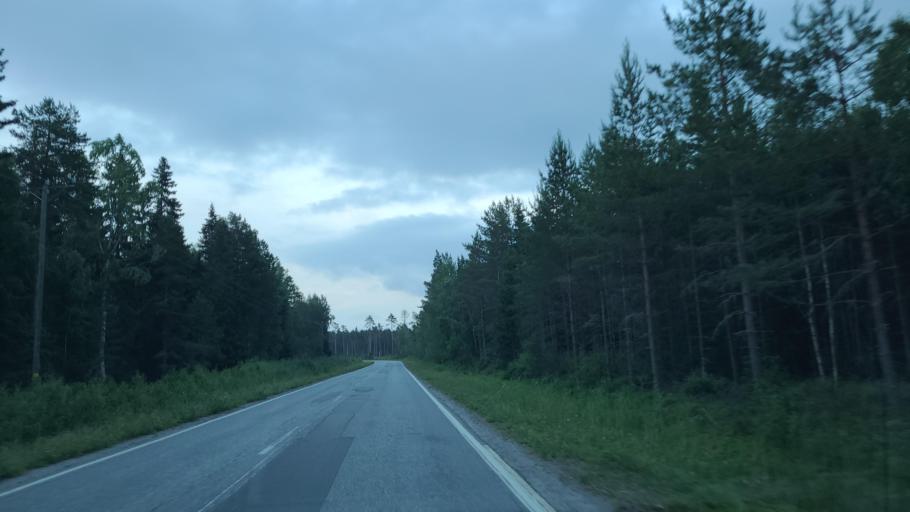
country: FI
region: Ostrobothnia
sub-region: Vaasa
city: Replot
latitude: 63.2052
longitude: 21.2673
